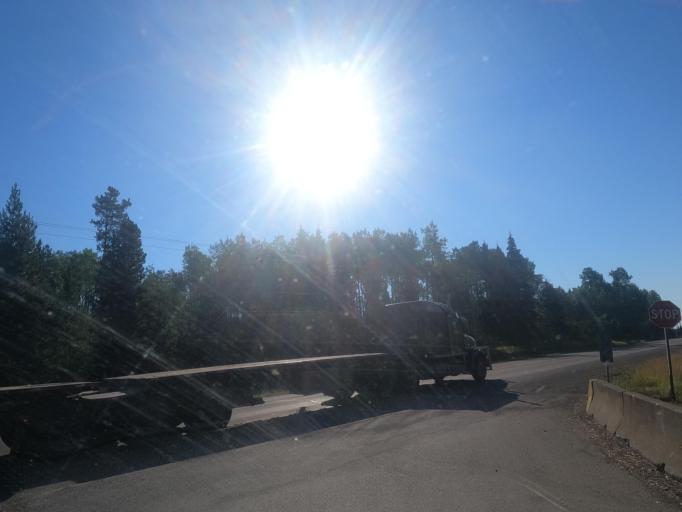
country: CA
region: British Columbia
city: Burns Lake
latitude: 54.3562
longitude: -125.9198
